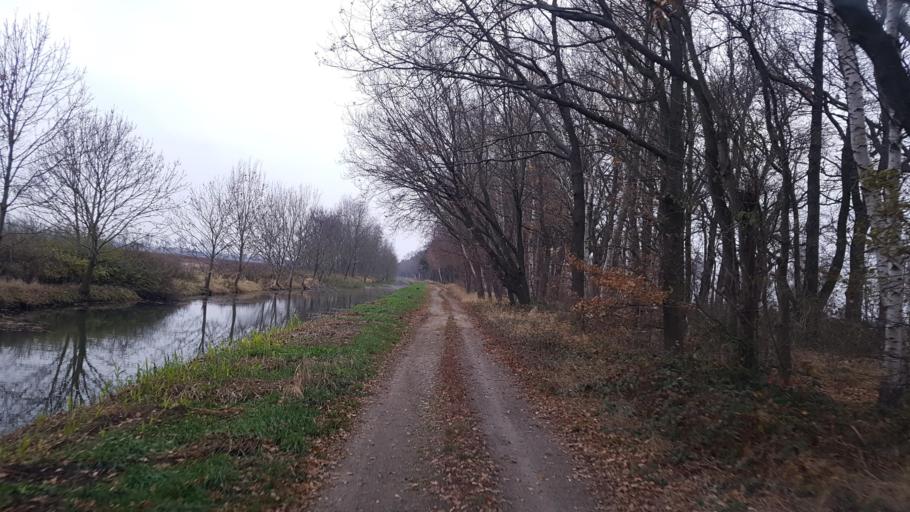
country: DE
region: Brandenburg
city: Hirschfeld
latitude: 51.4098
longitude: 13.6352
